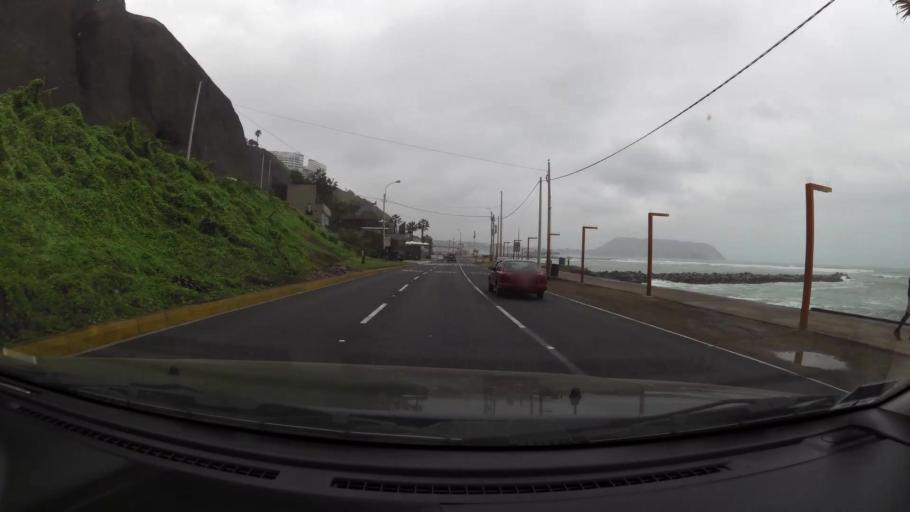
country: PE
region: Lima
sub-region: Lima
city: San Isidro
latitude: -12.1258
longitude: -77.0387
